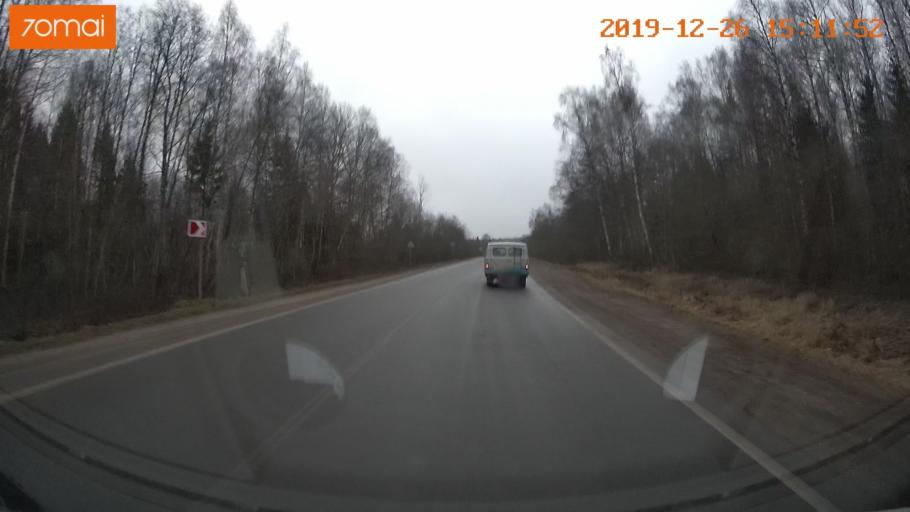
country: RU
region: Jaroslavl
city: Rybinsk
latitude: 58.1322
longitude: 38.8680
